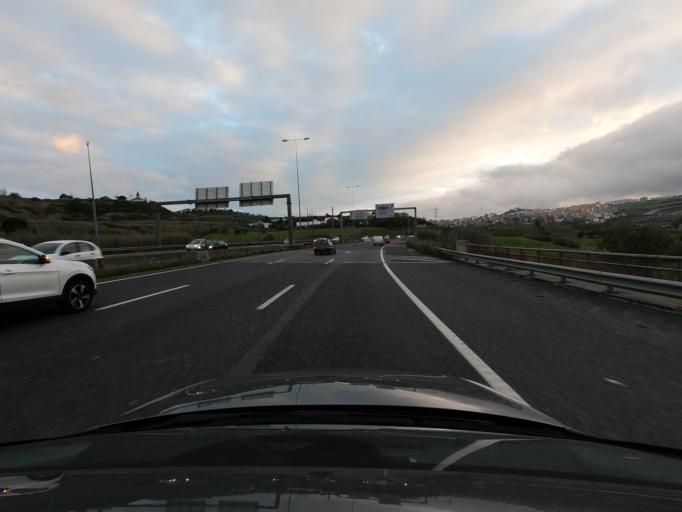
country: PT
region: Lisbon
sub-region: Odivelas
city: Pontinha
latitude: 38.7747
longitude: -9.1974
